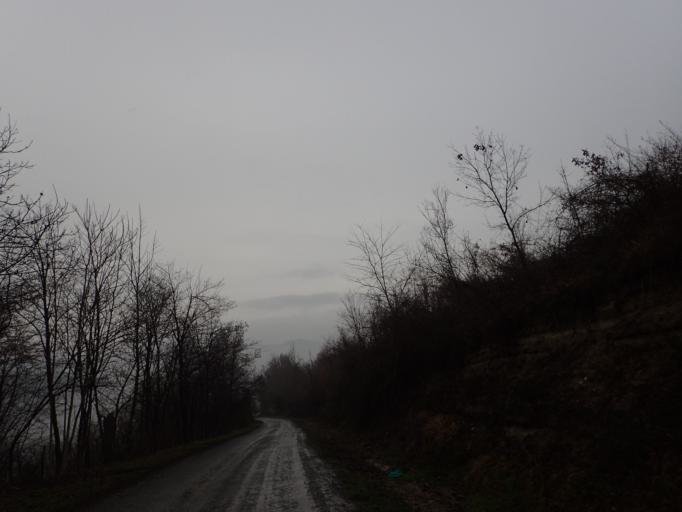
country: TR
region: Ordu
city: Camas
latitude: 40.9483
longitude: 37.5093
